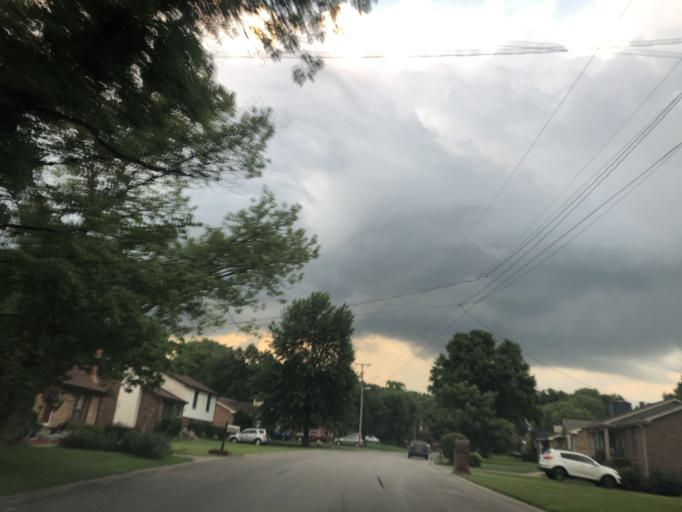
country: US
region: Tennessee
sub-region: Davidson County
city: Lakewood
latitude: 36.1487
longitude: -86.6308
